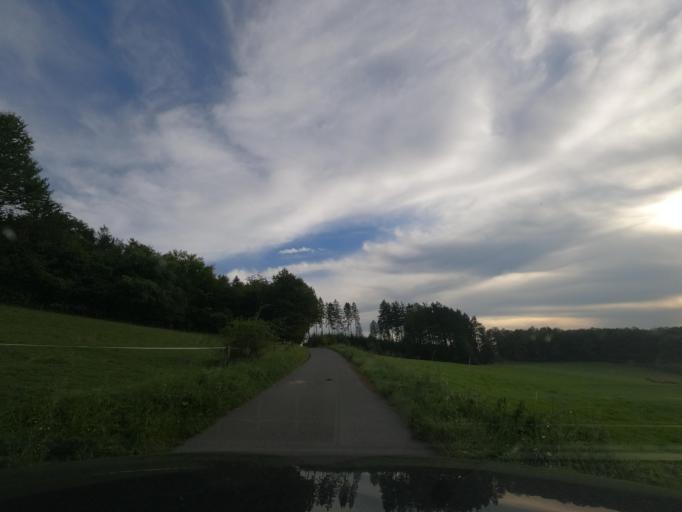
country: DE
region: North Rhine-Westphalia
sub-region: Regierungsbezirk Arnsberg
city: Herscheid
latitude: 51.2001
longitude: 7.7503
